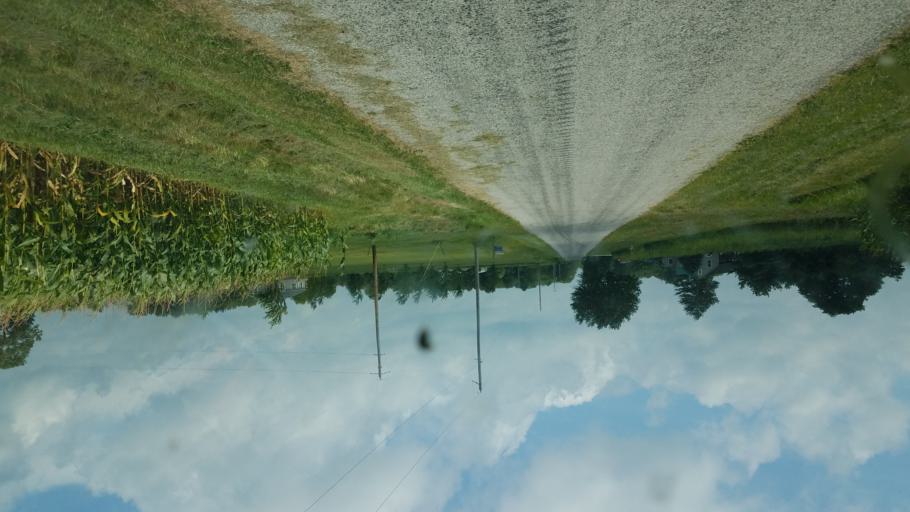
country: US
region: Ohio
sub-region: Richland County
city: Lexington
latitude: 40.6163
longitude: -82.6993
